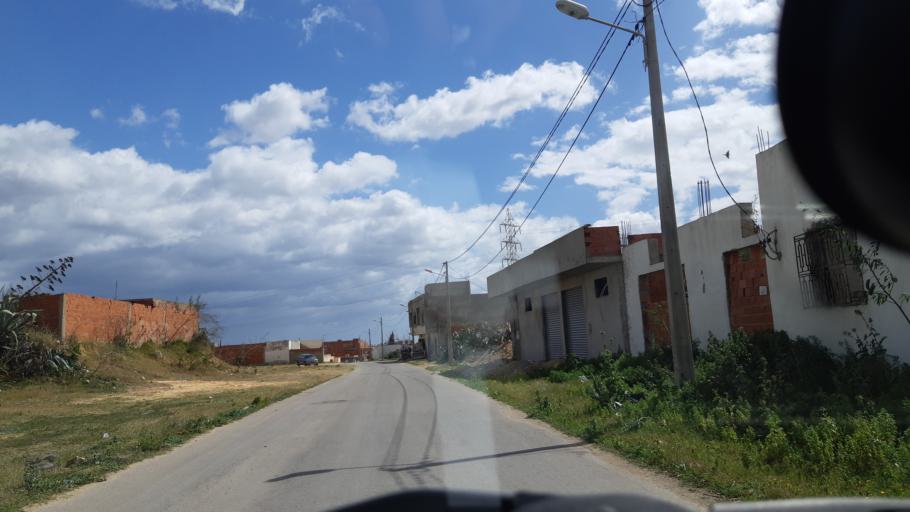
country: TN
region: Susah
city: Akouda
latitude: 35.8790
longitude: 10.5125
